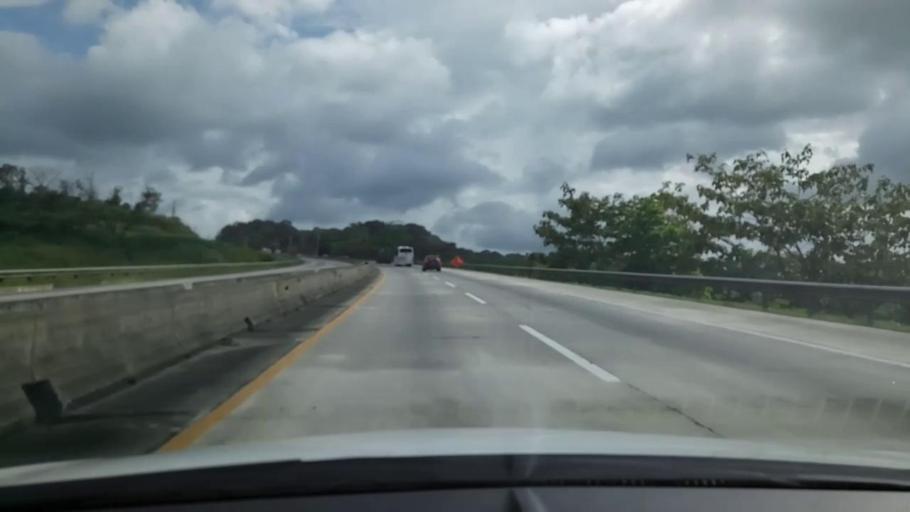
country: PA
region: Panama
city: Chilibre
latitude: 9.1294
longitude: -79.6221
